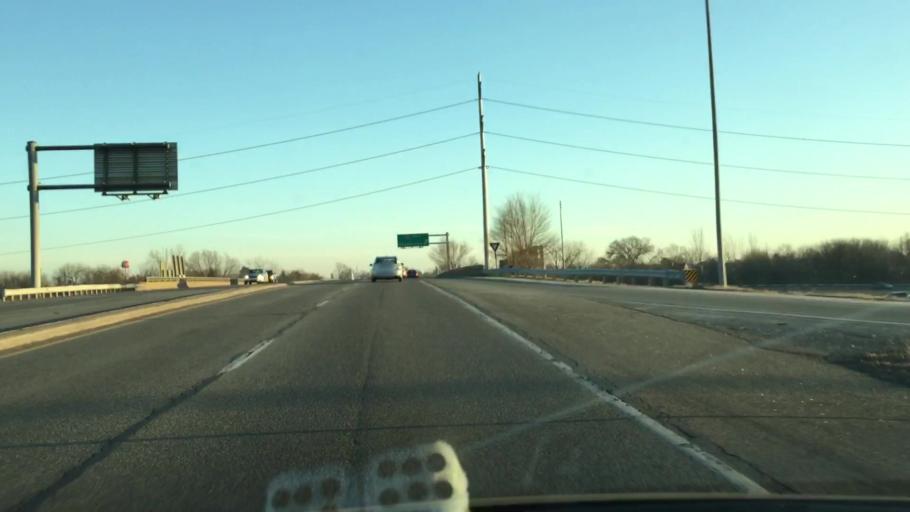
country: US
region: Pennsylvania
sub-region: Delaware County
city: Prospect Park
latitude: 39.8717
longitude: -75.3019
